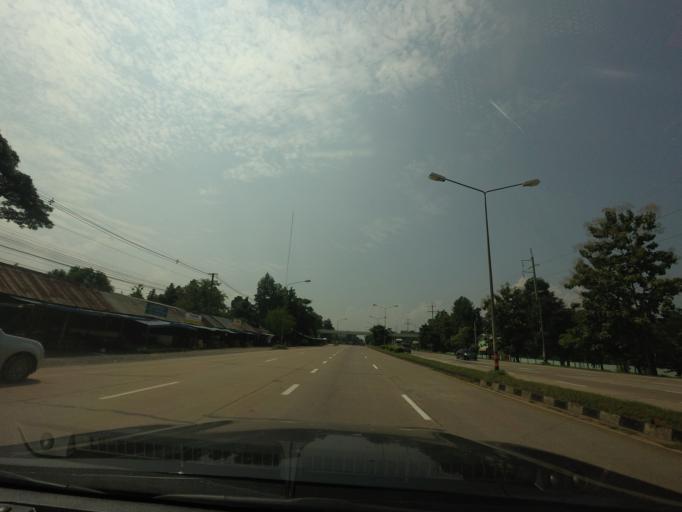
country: TH
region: Phrae
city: Den Chai
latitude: 17.9827
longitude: 100.0929
